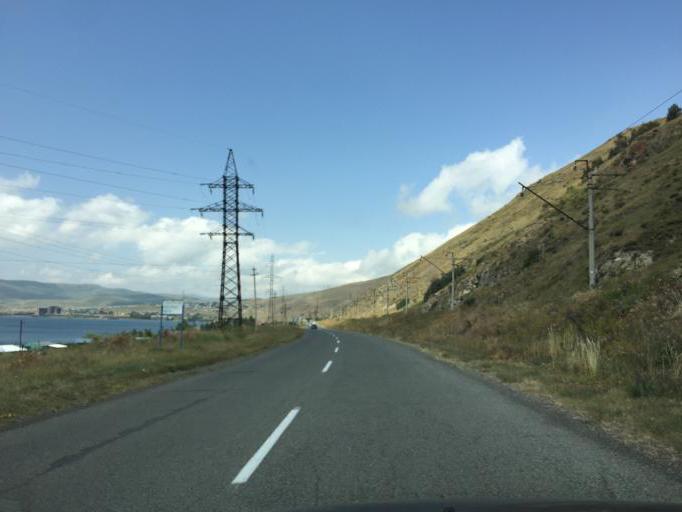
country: AM
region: Geghark'unik'i Marz
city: Tsovagyugh
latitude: 40.6265
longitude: 45.0086
